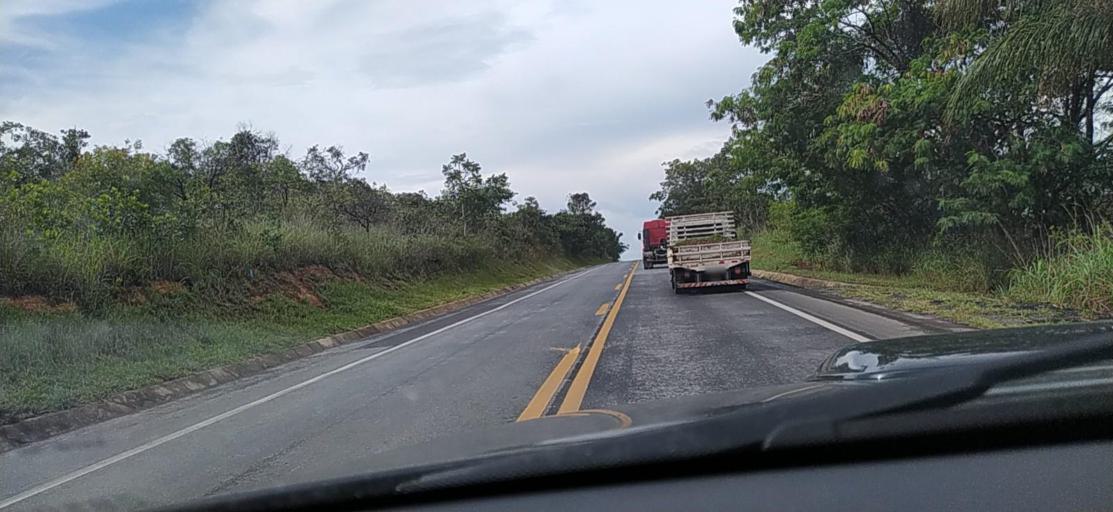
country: BR
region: Minas Gerais
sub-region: Montes Claros
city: Montes Claros
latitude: -16.8511
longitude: -43.8522
